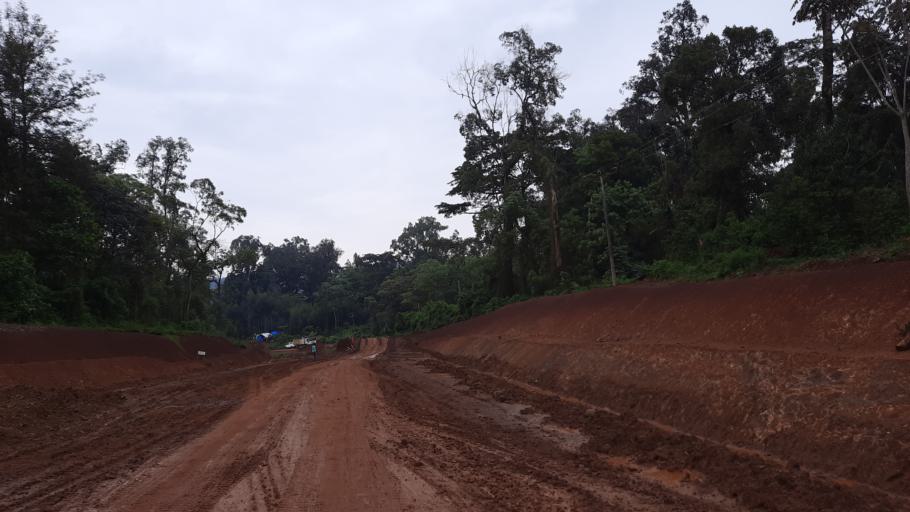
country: ET
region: Oromiya
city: Gore
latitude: 7.8637
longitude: 35.4786
